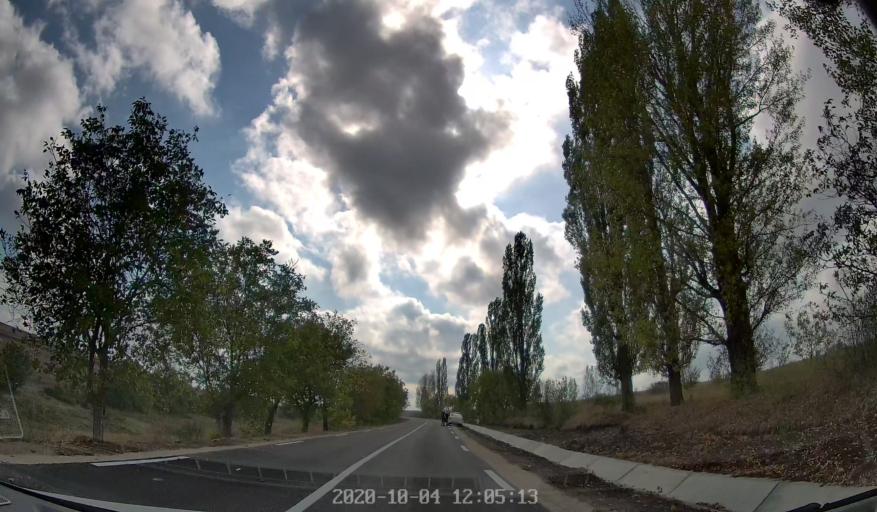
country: MD
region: Rezina
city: Saharna
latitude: 47.5959
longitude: 28.9493
